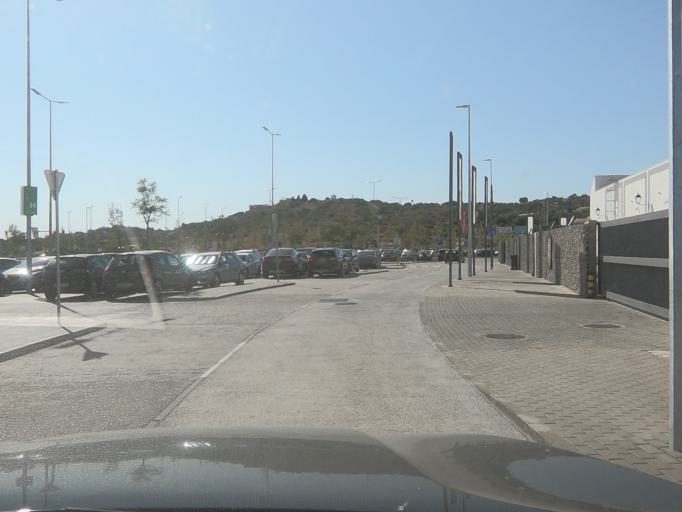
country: PT
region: Faro
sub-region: Loule
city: Almancil
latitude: 37.0991
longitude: -8.0004
